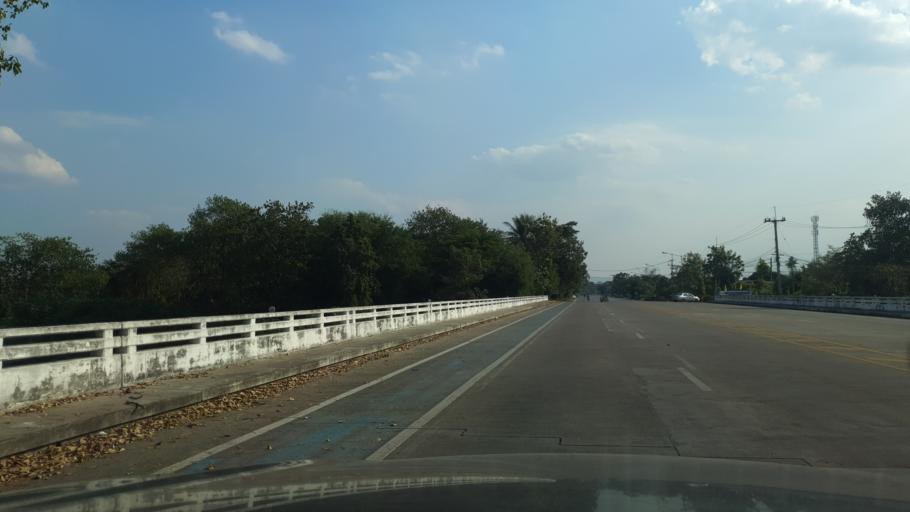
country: TH
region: Tak
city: Tak
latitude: 16.8662
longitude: 99.1199
